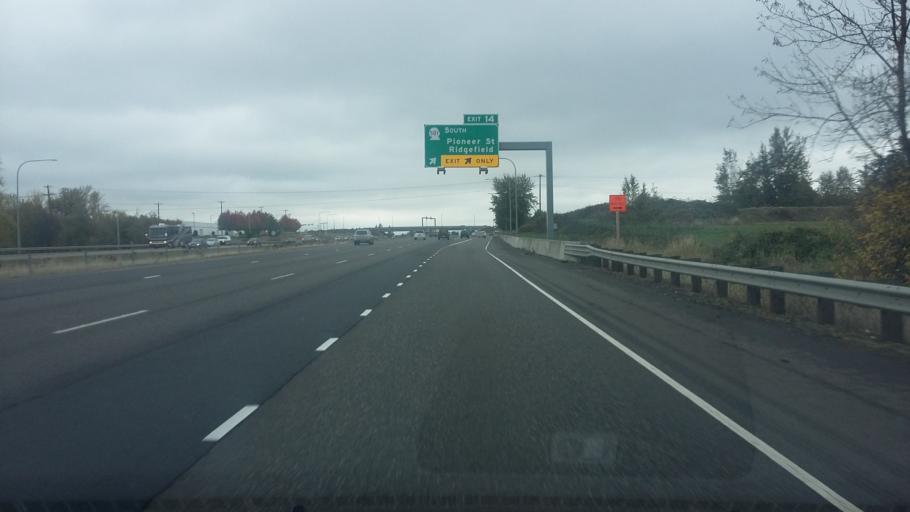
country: US
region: Washington
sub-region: Clark County
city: La Center
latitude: 45.8104
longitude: -122.6831
